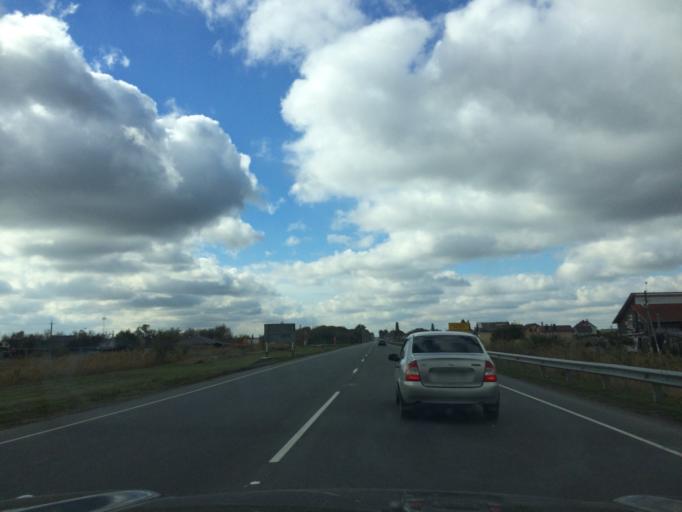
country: RU
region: Rostov
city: Bataysk
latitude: 47.1132
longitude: 39.6590
